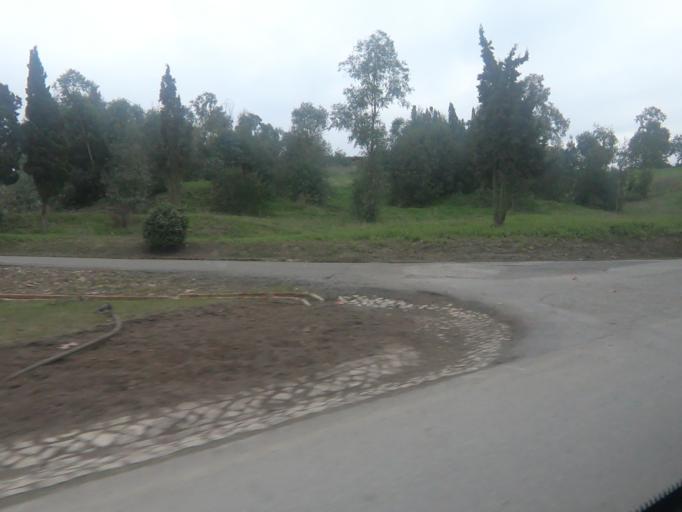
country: PT
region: Setubal
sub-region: Setubal
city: Setubal
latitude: 38.4968
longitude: -8.8322
